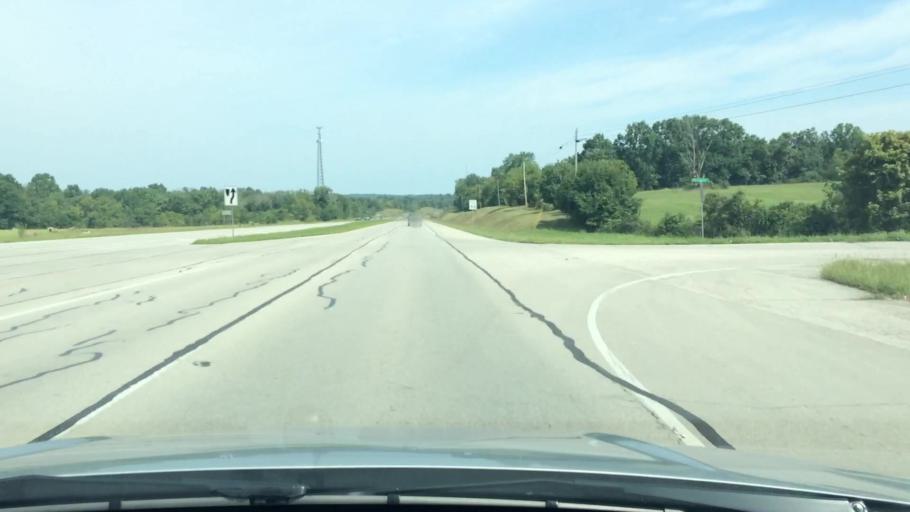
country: US
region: Kentucky
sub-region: Anderson County
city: Lawrenceburg
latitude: 38.0873
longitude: -84.9186
